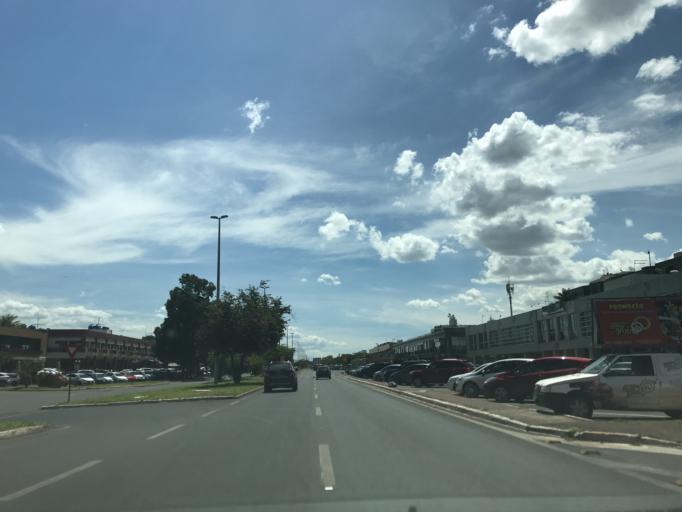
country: BR
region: Federal District
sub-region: Brasilia
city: Brasilia
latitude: -15.7972
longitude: -47.9191
